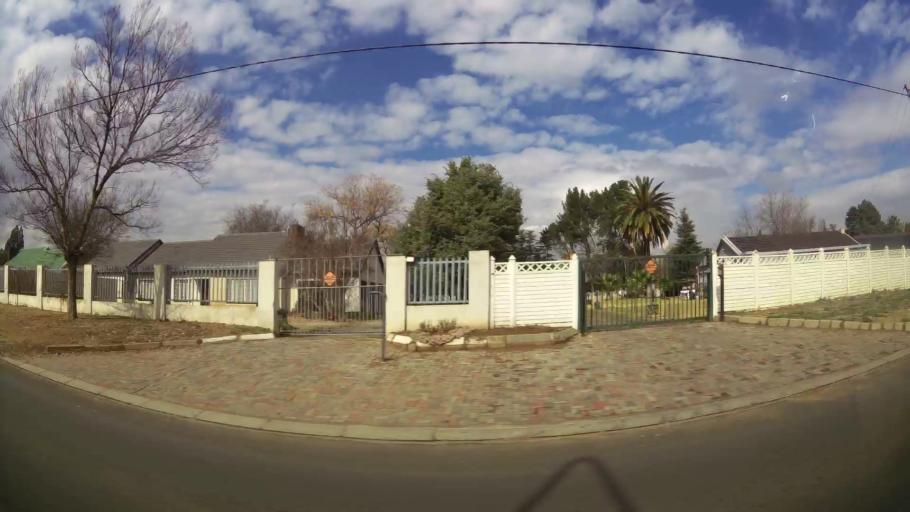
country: ZA
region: Gauteng
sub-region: Sedibeng District Municipality
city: Vereeniging
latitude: -26.6612
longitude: 27.9802
